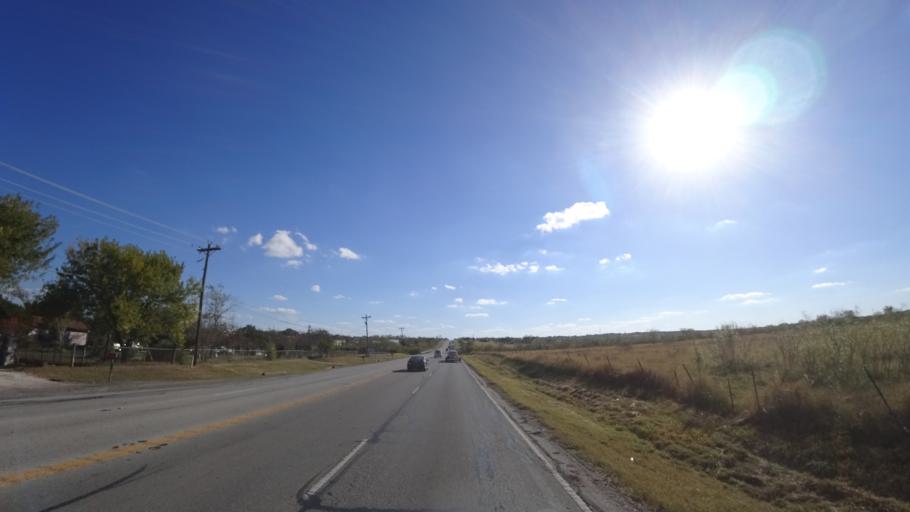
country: US
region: Texas
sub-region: Travis County
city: Onion Creek
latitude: 30.1327
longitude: -97.6961
